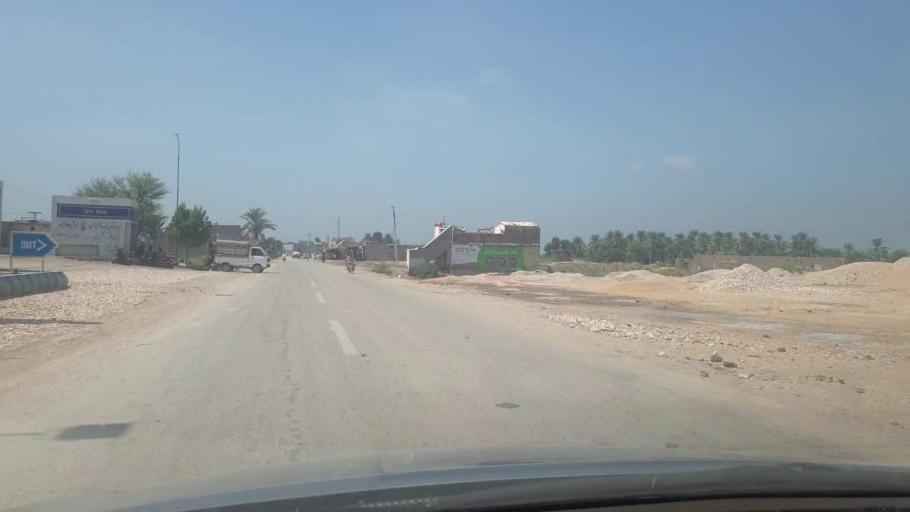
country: PK
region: Sindh
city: Bozdar
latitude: 27.2251
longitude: 68.5667
